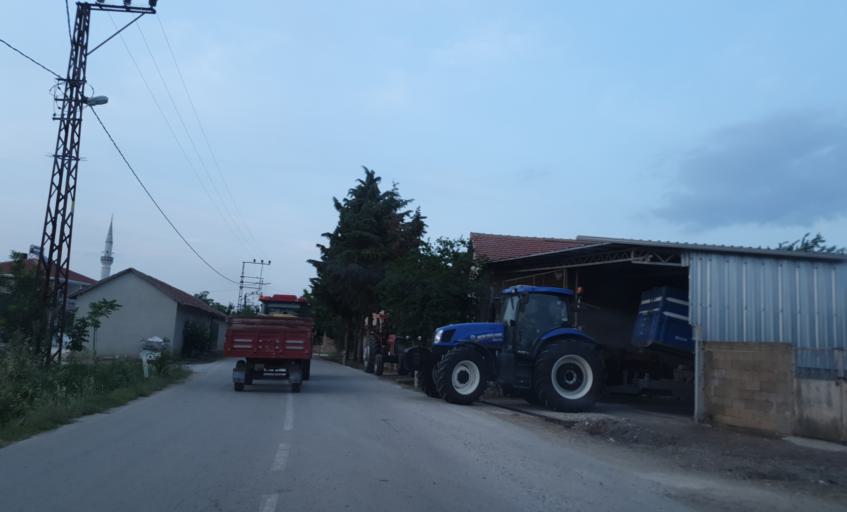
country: TR
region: Tekirdag
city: Beyazkoy
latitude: 41.4104
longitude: 27.6529
